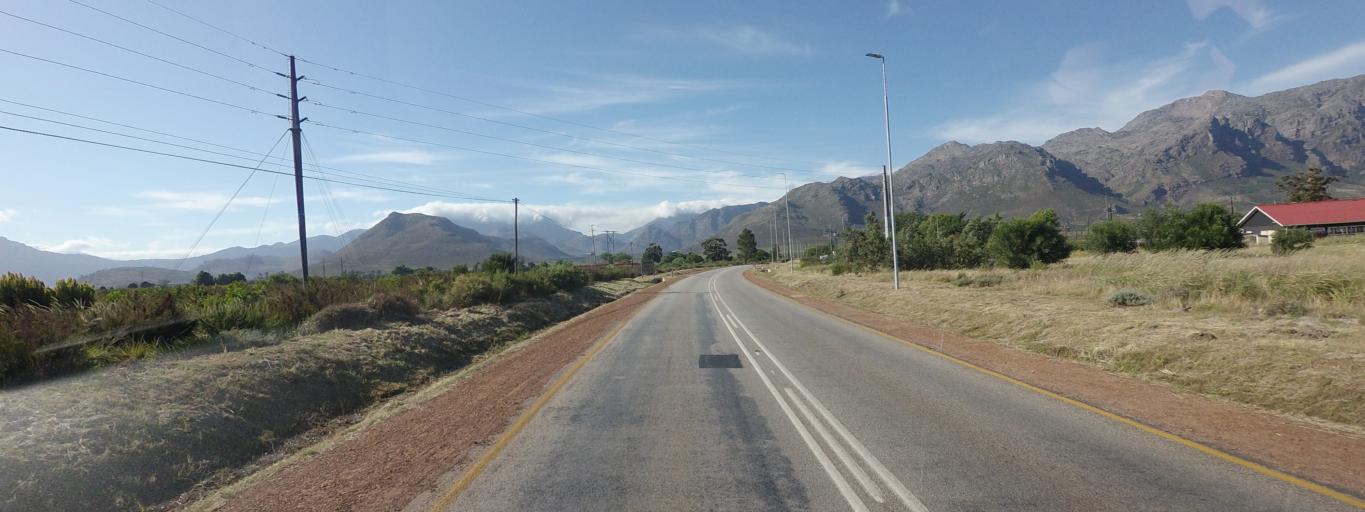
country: ZA
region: Western Cape
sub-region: Cape Winelands District Municipality
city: Paarl
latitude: -33.8734
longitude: 19.0446
